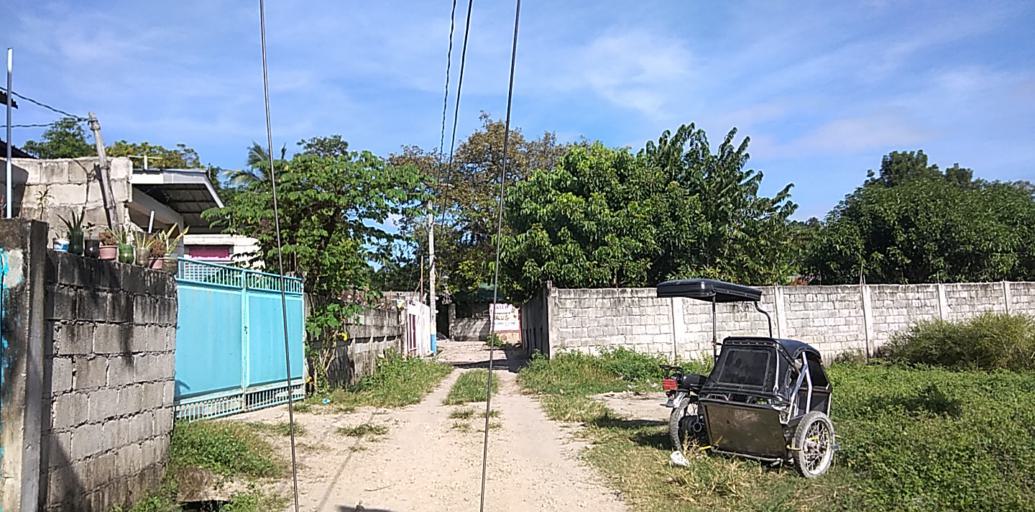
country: PH
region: Central Luzon
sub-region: Province of Pampanga
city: Porac
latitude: 15.0784
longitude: 120.5388
